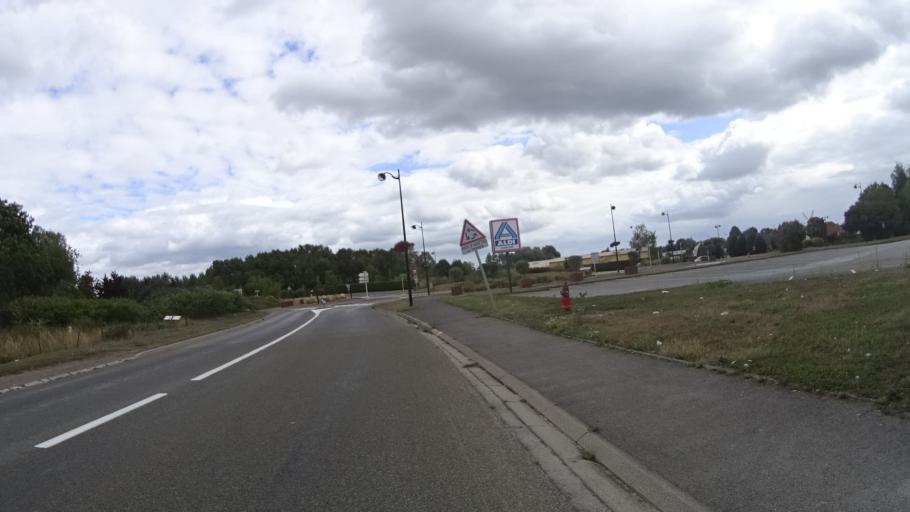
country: FR
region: Picardie
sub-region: Departement de l'Aisne
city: Beautor
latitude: 49.6626
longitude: 3.3489
